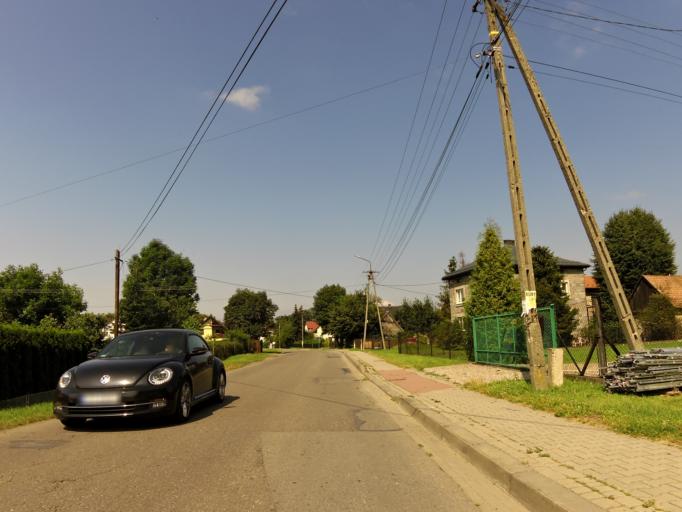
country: PL
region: Silesian Voivodeship
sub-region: Powiat zywiecki
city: Wieprz
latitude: 49.6347
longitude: 19.1725
